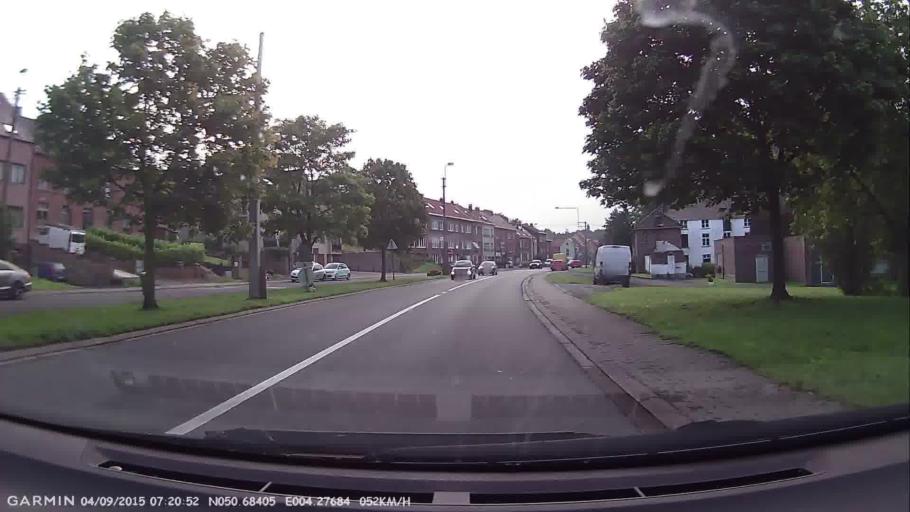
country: BE
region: Wallonia
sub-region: Province du Brabant Wallon
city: Braine-le-Chateau
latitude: 50.6841
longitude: 4.2770
